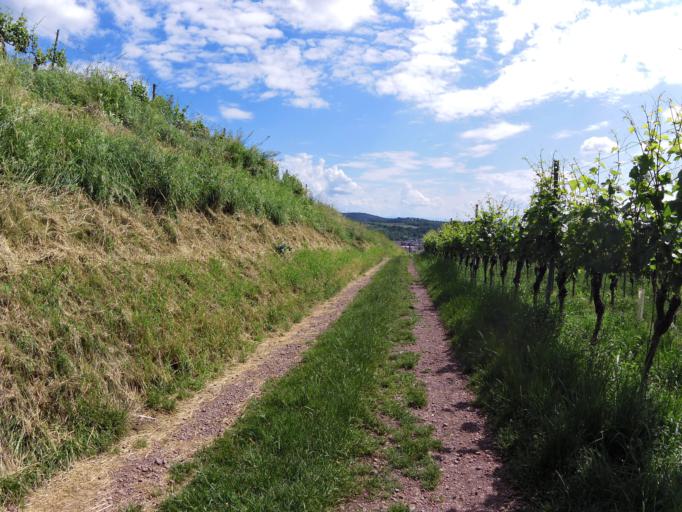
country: DE
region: Baden-Wuerttemberg
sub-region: Freiburg Region
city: Lahr
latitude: 48.3458
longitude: 7.8496
